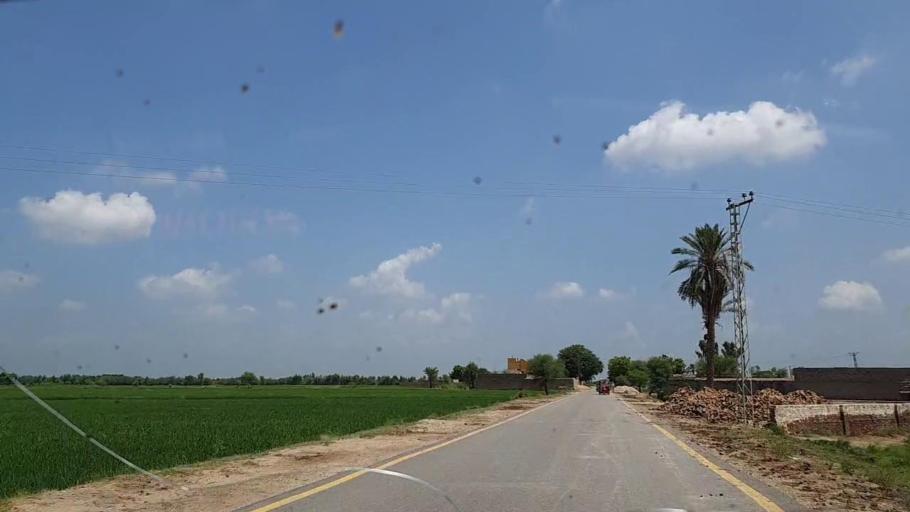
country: PK
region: Sindh
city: Tharu Shah
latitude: 26.9795
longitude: 68.0837
